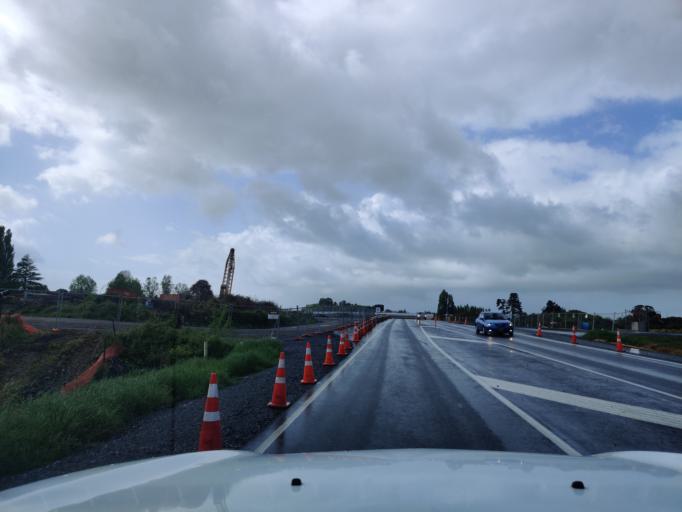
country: NZ
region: Waikato
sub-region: Hamilton City
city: Hamilton
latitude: -37.8136
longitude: 175.3409
